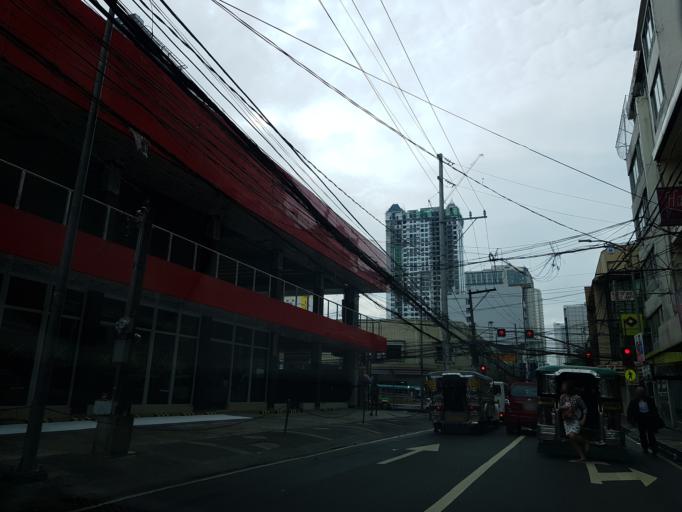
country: PH
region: Metro Manila
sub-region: City of Manila
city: Port Area
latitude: 14.5773
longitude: 120.9803
